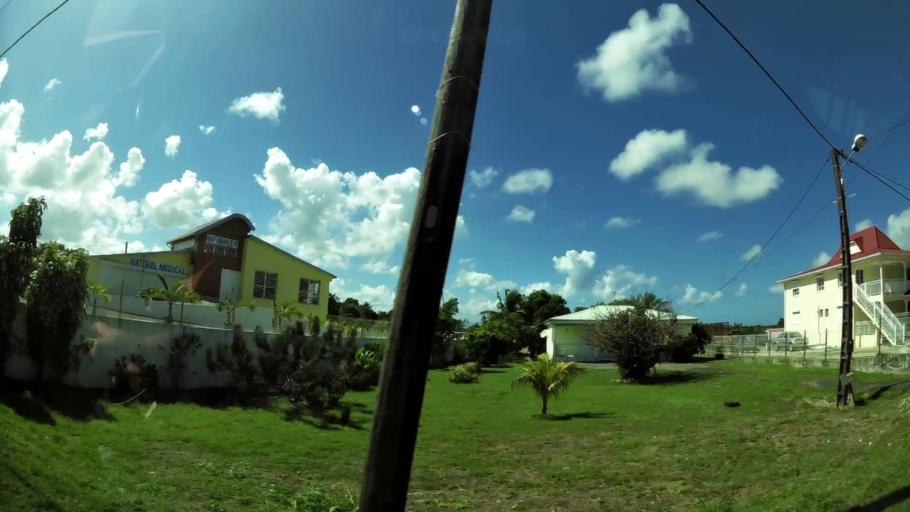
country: GP
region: Guadeloupe
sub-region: Guadeloupe
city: Petit-Canal
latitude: 16.3853
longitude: -61.4579
